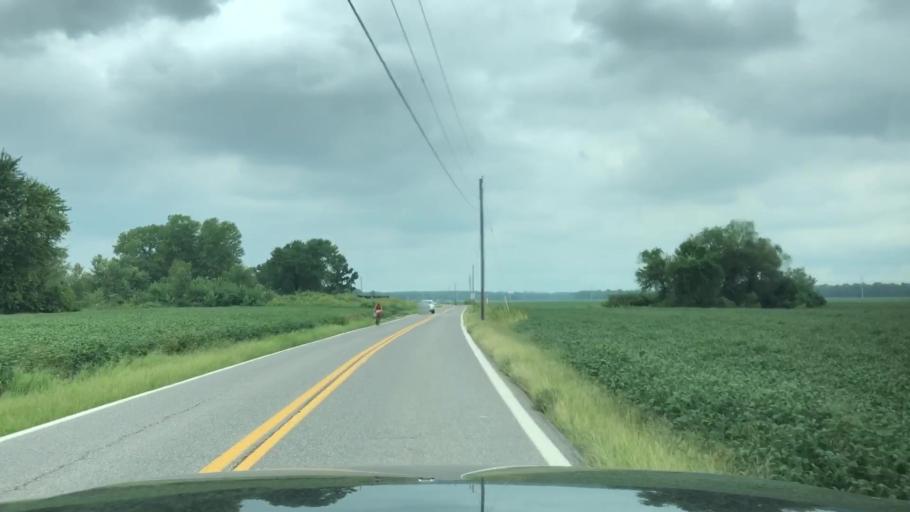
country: US
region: Missouri
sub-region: Saint Louis County
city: Bridgeton
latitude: 38.7972
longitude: -90.4231
